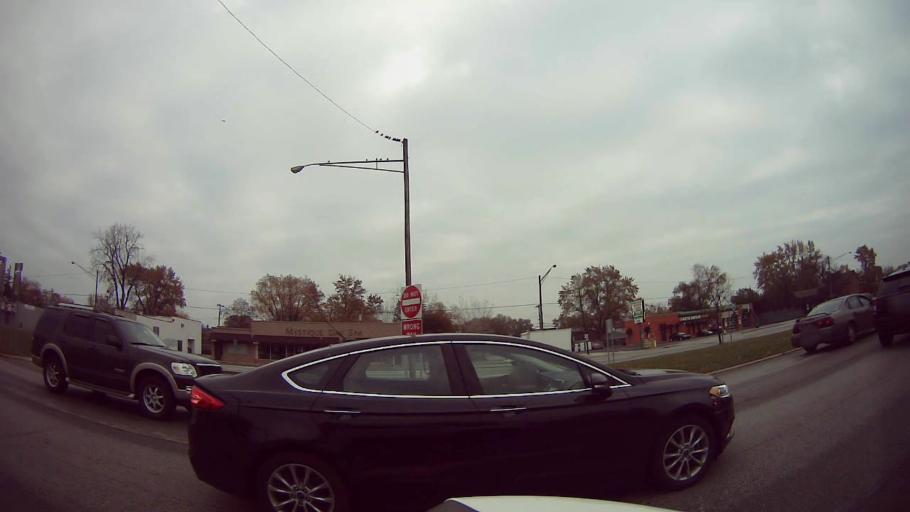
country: US
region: Michigan
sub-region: Wayne County
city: Dearborn Heights
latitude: 42.3159
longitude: -83.2724
